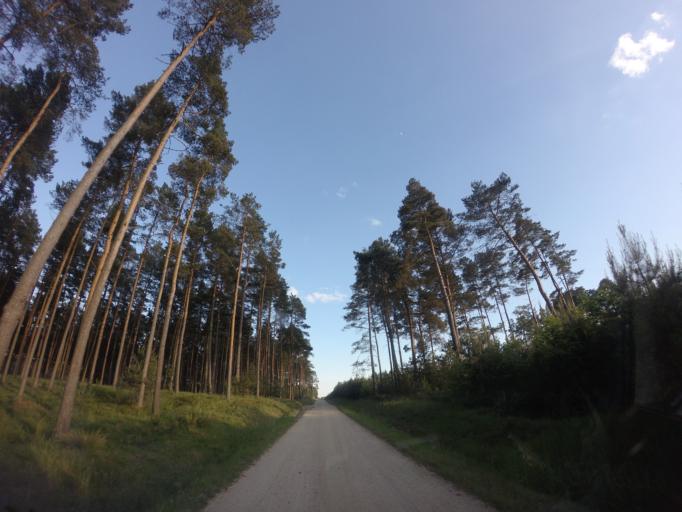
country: PL
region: West Pomeranian Voivodeship
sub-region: Powiat choszczenski
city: Drawno
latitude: 53.1539
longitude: 15.7285
